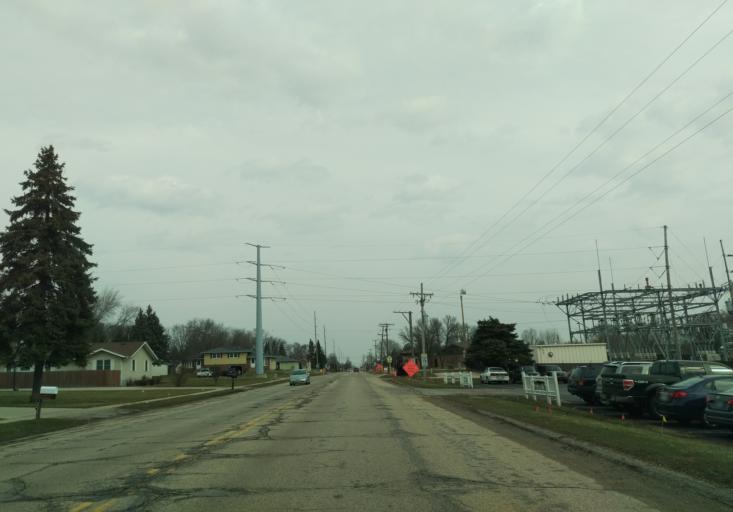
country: US
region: Wisconsin
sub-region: Dane County
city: Waunakee
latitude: 43.1838
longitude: -89.4617
